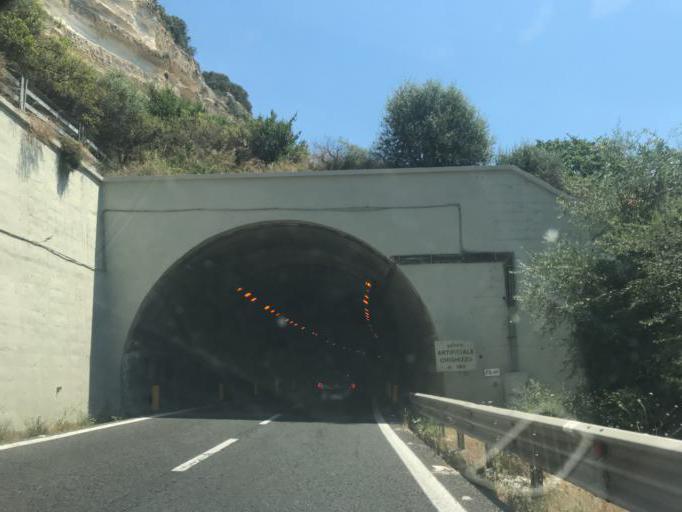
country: IT
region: Sardinia
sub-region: Provincia di Sassari
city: Ossi
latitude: 40.7011
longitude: 8.5852
